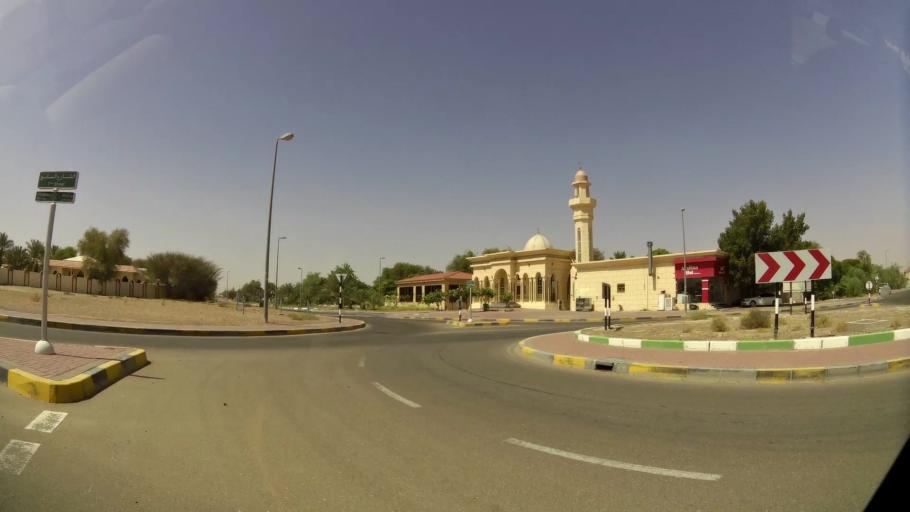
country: OM
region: Al Buraimi
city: Al Buraymi
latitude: 24.2879
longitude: 55.7607
